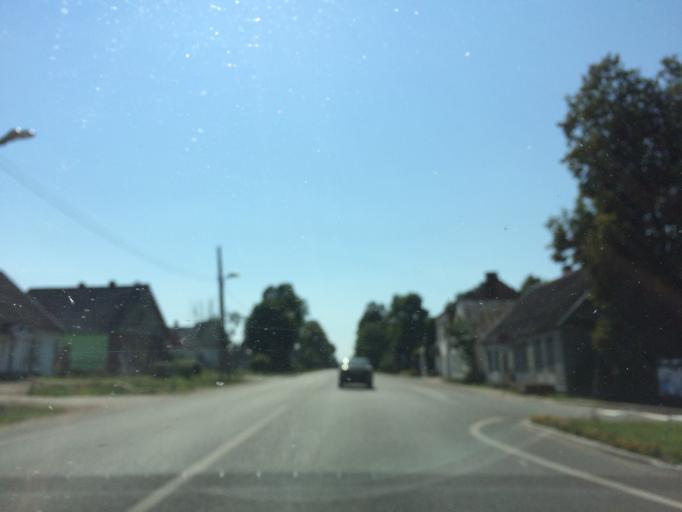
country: LV
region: Rezekne
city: Rezekne
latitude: 56.3449
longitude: 27.1605
